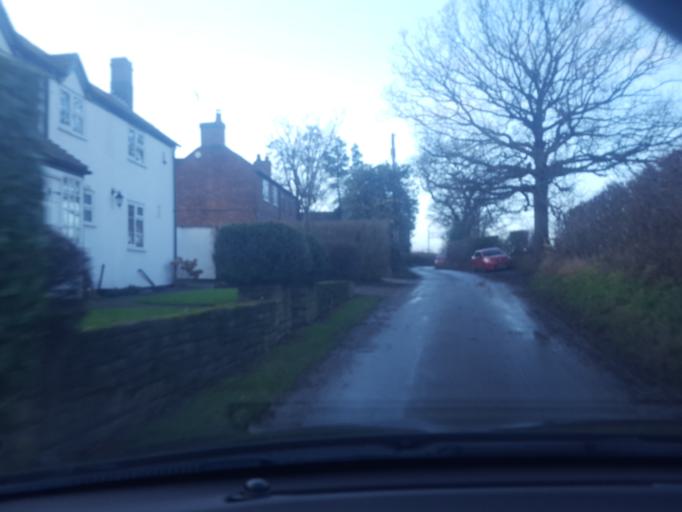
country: GB
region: England
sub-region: Staffordshire
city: Codsall
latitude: 52.6359
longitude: -2.2327
